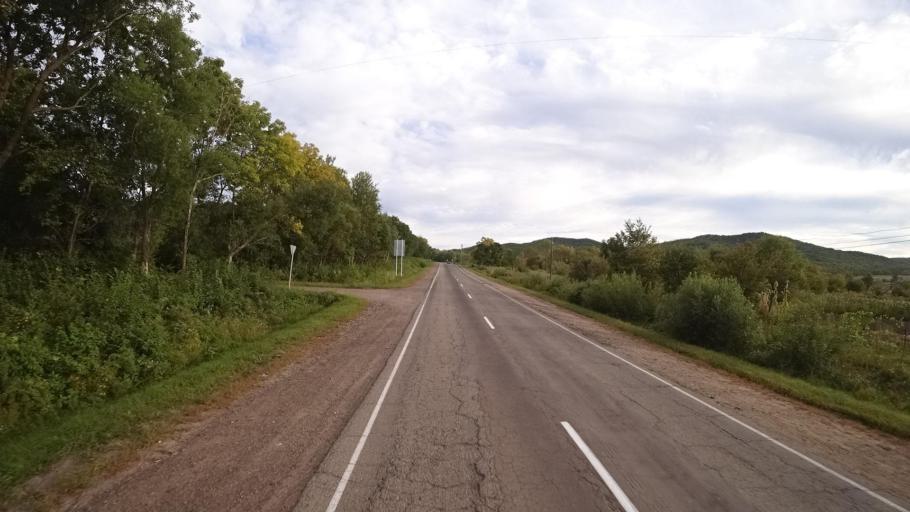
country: RU
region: Primorskiy
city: Yakovlevka
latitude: 44.4151
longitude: 133.4532
